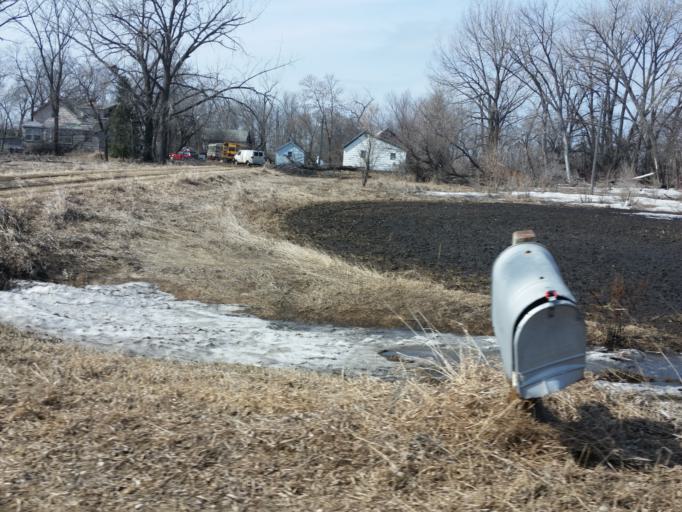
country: US
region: North Dakota
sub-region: Walsh County
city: Grafton
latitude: 48.2821
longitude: -97.2546
